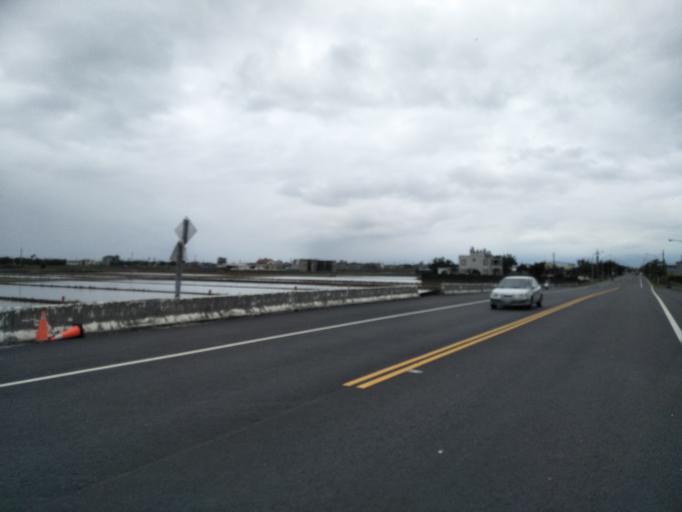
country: TW
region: Taiwan
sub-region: Yilan
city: Yilan
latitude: 24.8072
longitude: 121.7905
